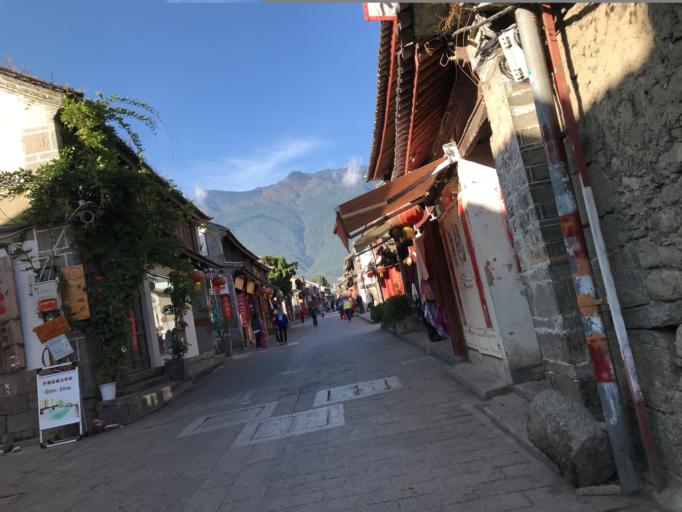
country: CN
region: Yunnan
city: Dali
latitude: 25.6978
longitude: 100.1652
